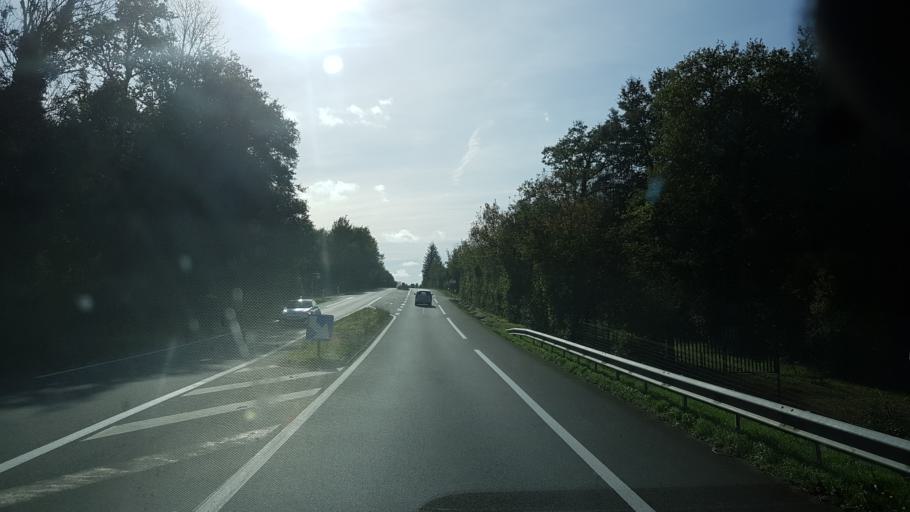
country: FR
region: Poitou-Charentes
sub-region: Departement de la Charente
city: Loubert
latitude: 45.9592
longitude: 0.5768
